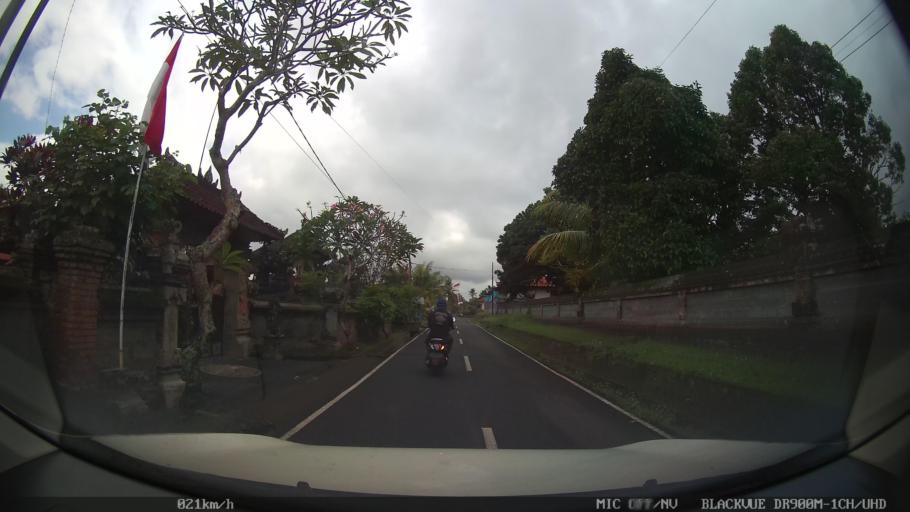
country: ID
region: Bali
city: Banjar Mambalkajanan
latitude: -8.5525
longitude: 115.2107
